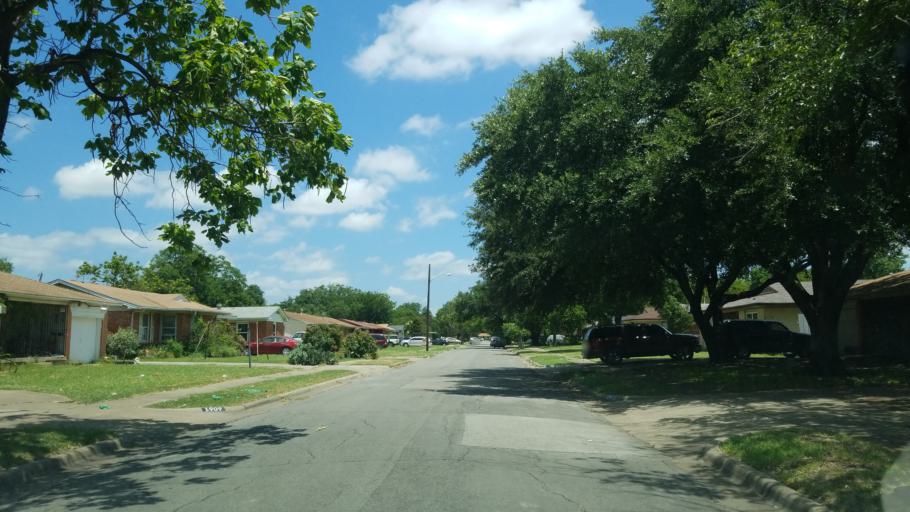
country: US
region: Texas
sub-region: Dallas County
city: Balch Springs
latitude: 32.7449
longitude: -96.6973
